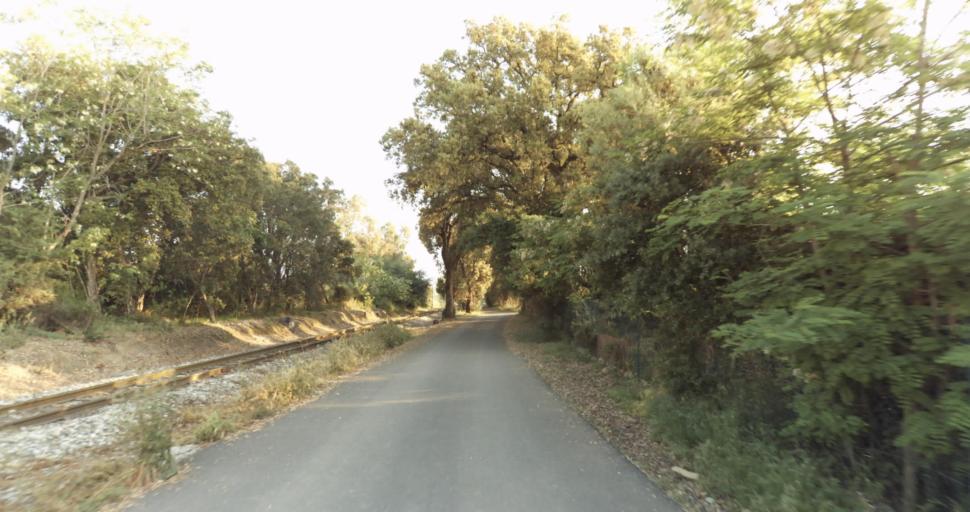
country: FR
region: Corsica
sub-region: Departement de la Haute-Corse
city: Biguglia
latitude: 42.6303
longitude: 9.4407
